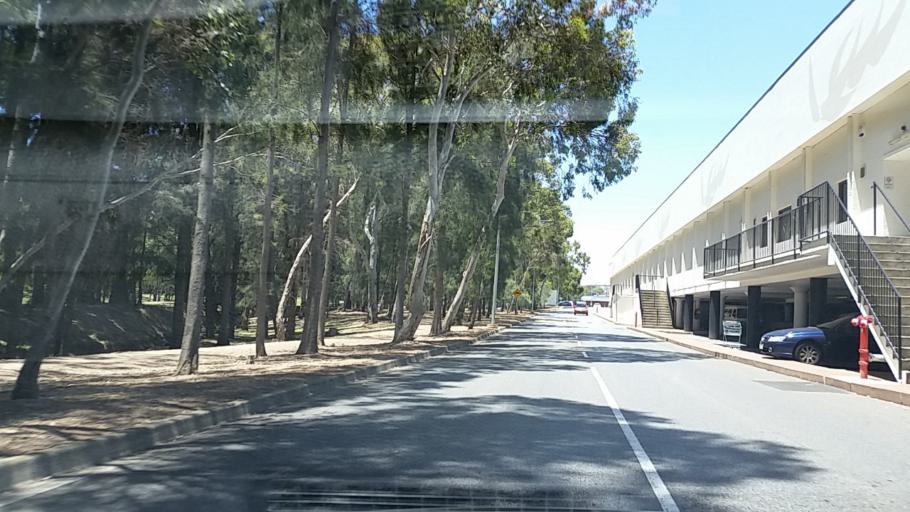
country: AU
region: South Australia
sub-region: Salisbury
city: Salisbury
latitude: -34.7594
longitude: 138.6454
